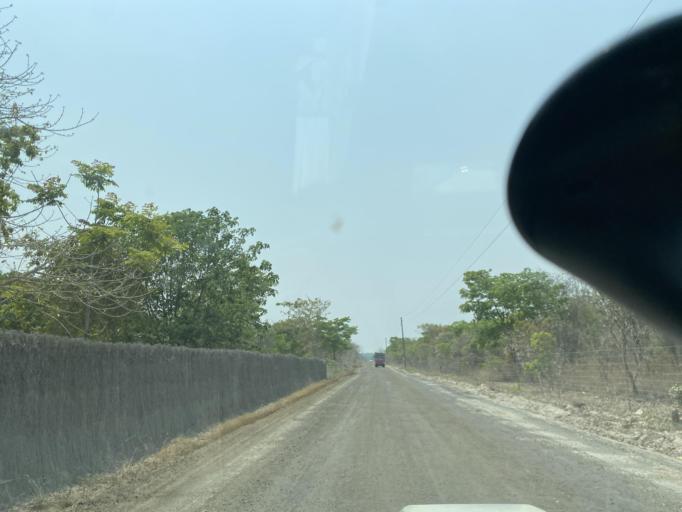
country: ZM
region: Lusaka
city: Lusaka
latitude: -15.5216
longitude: 28.4441
